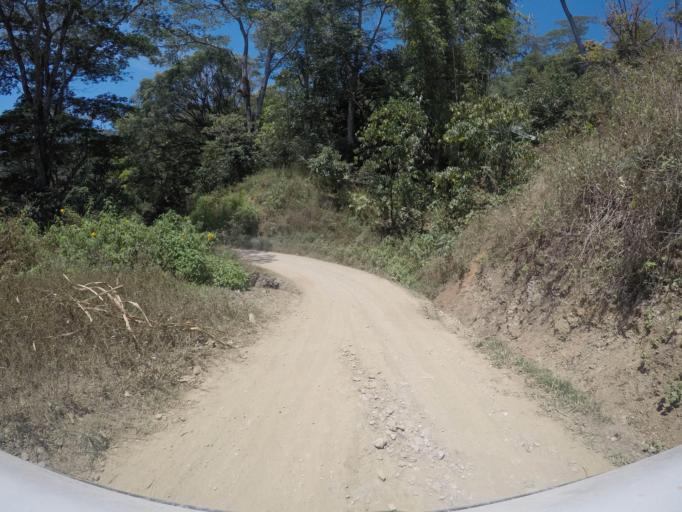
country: TL
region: Ermera
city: Gleno
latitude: -8.7414
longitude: 125.4044
